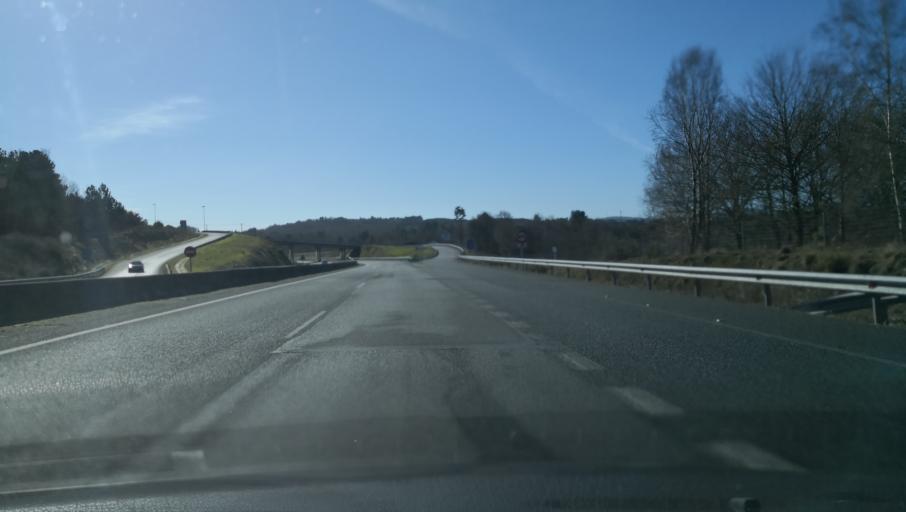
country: ES
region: Galicia
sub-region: Provincia de Pontevedra
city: Lalin
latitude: 42.6415
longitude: -8.1325
